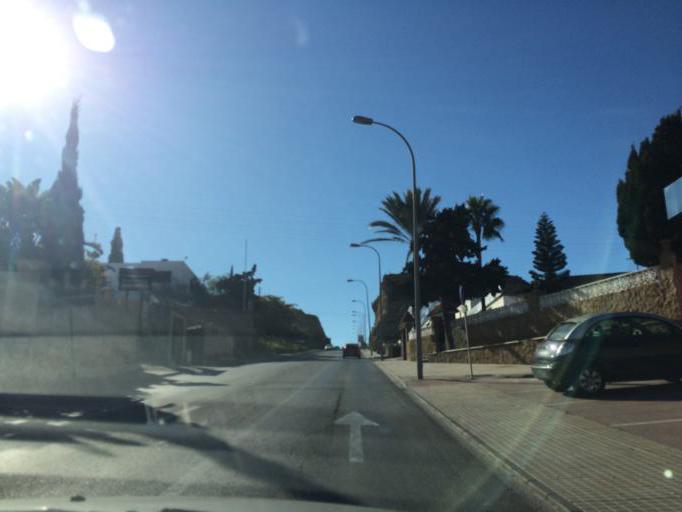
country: ES
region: Andalusia
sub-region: Provincia de Almeria
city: Huercal de Almeria
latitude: 36.8662
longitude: -2.4415
